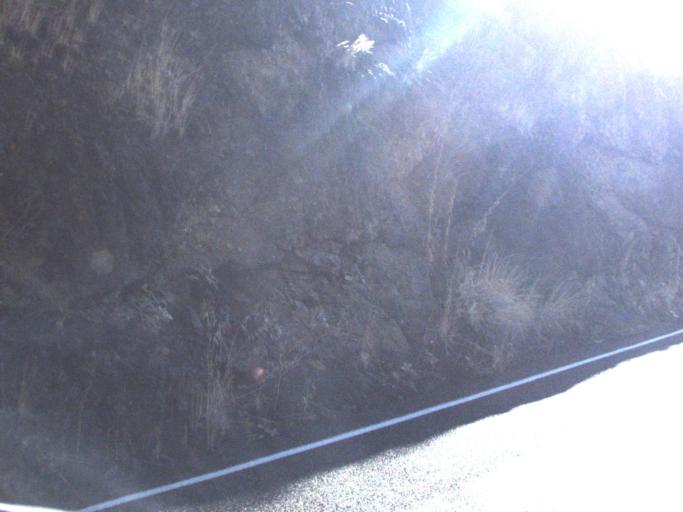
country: US
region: Washington
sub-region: Asotin County
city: Asotin
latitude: 46.0526
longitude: -117.2381
